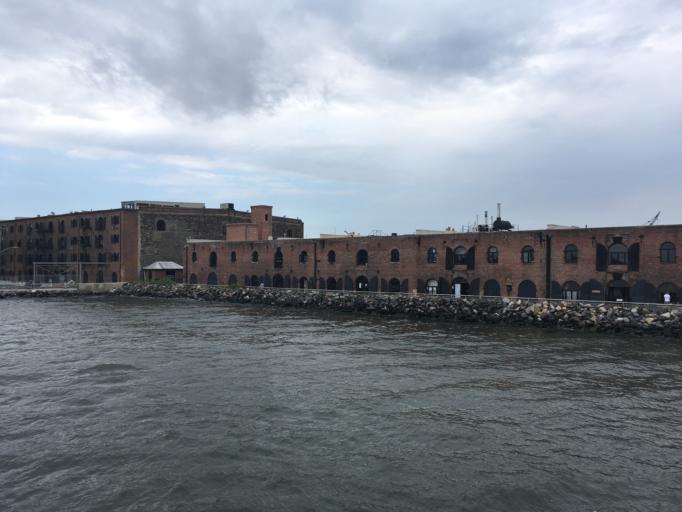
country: US
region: New York
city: New York City
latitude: 40.6732
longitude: -74.0185
